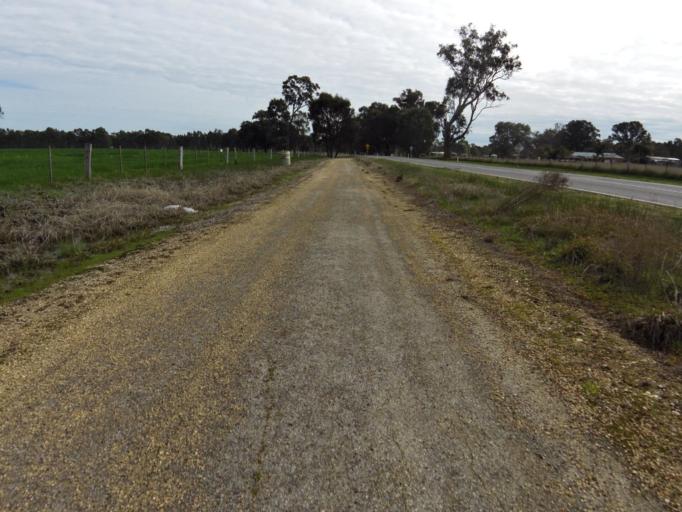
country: AU
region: Victoria
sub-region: Wangaratta
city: Wangaratta
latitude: -36.3982
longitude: 146.3454
